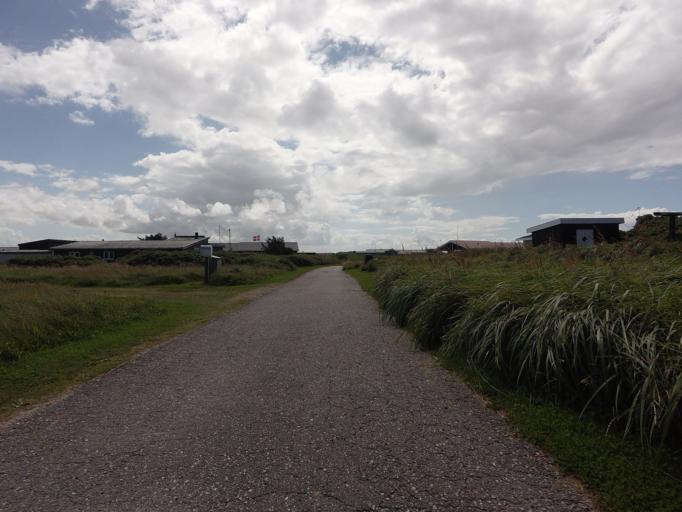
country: DK
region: North Denmark
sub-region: Jammerbugt Kommune
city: Pandrup
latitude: 57.3593
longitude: 9.6988
